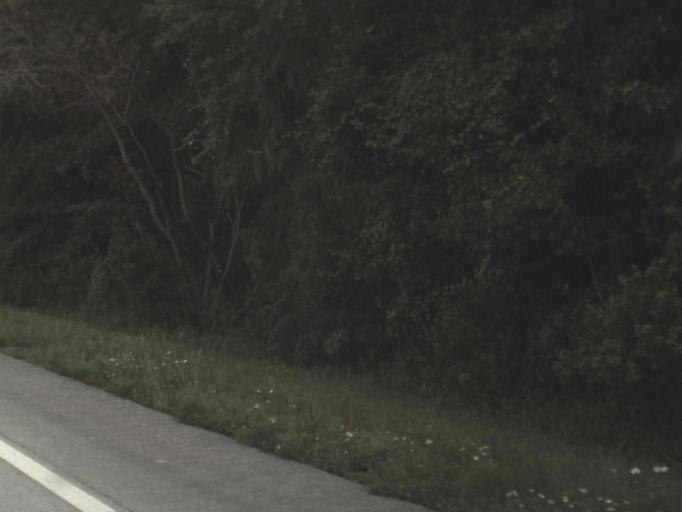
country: US
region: Florida
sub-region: Hardee County
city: Bowling Green
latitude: 27.5951
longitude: -82.0314
